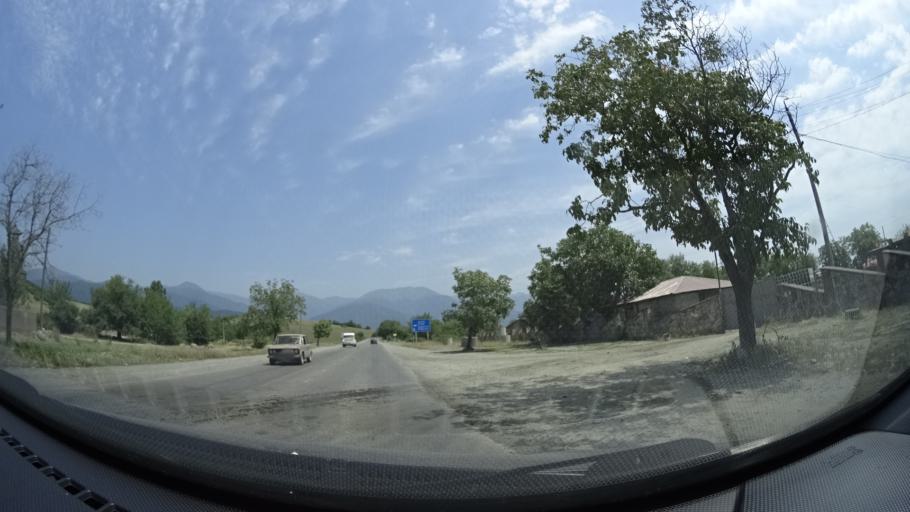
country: GE
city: Bagdadi
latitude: 41.8371
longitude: 46.0991
